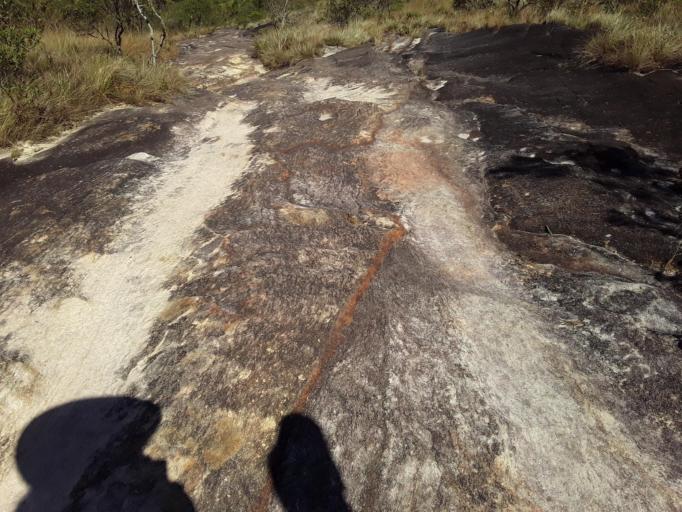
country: BR
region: Minas Gerais
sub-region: Lima Duarte
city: Lima Duarte
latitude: -21.7077
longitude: -43.8937
